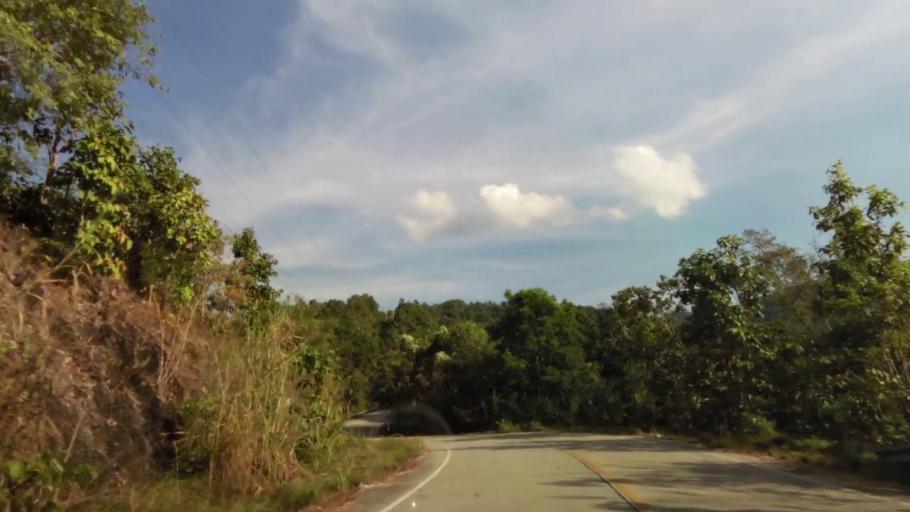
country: TH
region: Chiang Rai
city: Khun Tan
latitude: 19.8809
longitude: 100.3047
